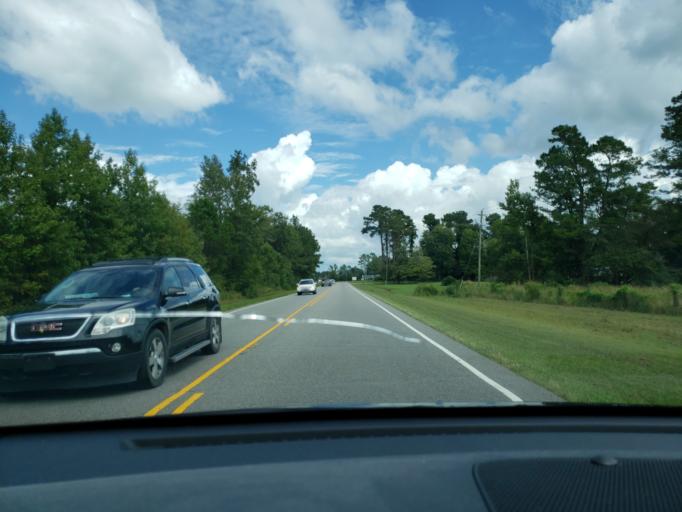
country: US
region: North Carolina
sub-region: Columbus County
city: Brunswick
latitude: 34.2132
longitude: -78.7579
